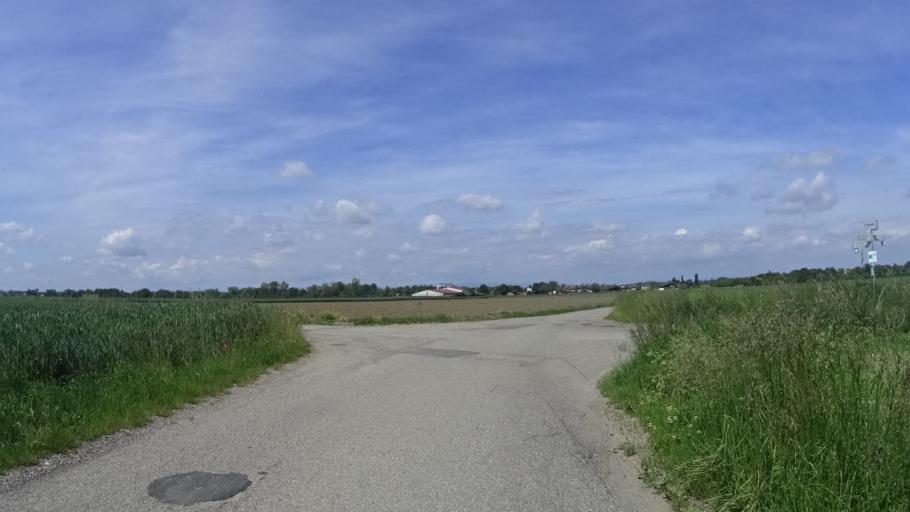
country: DE
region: Baden-Wuerttemberg
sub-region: Freiburg Region
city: Meissenheim
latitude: 48.4286
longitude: 7.7893
